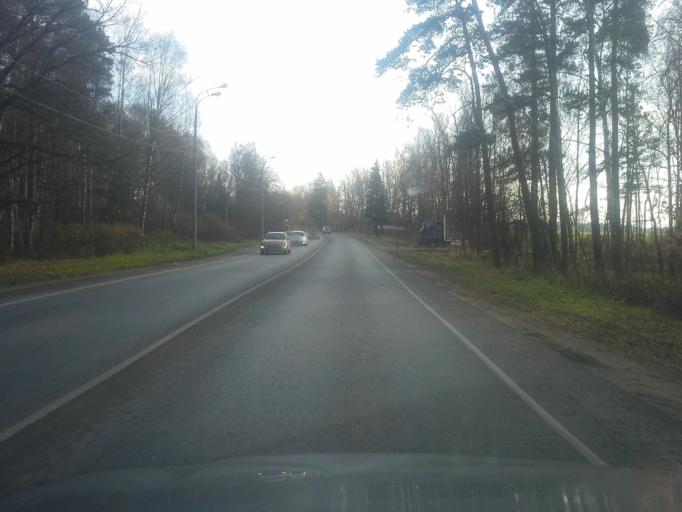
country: RU
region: Moskovskaya
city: Bol'shiye Vyazemy
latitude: 55.6689
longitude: 36.9552
